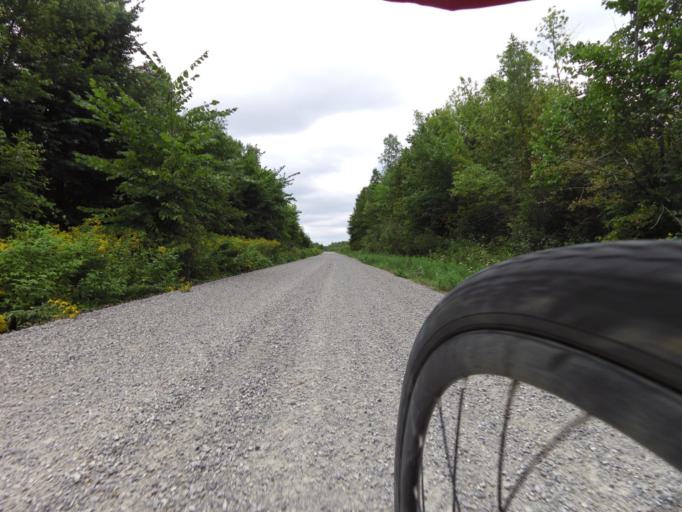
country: CA
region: Ontario
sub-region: Lanark County
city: Smiths Falls
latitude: 44.9520
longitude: -76.0450
